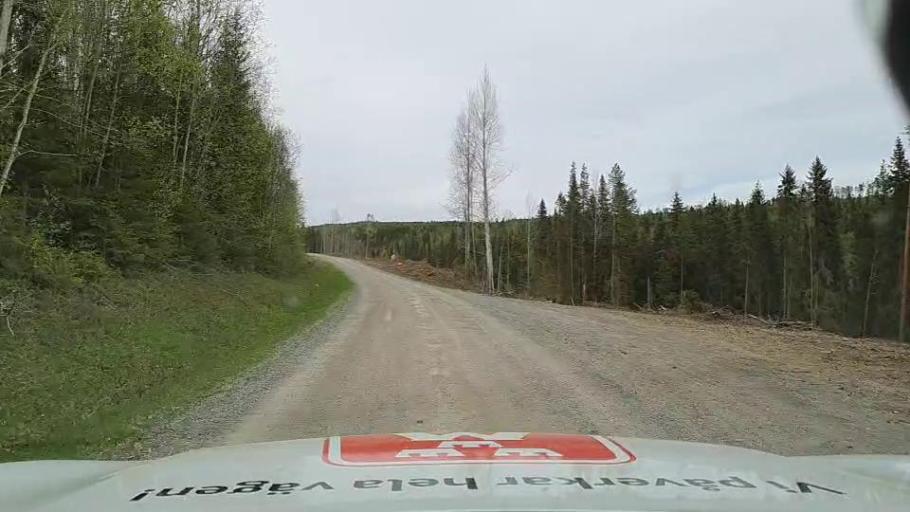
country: SE
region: Jaemtland
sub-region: Bergs Kommun
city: Hoverberg
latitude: 62.5239
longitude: 14.7102
